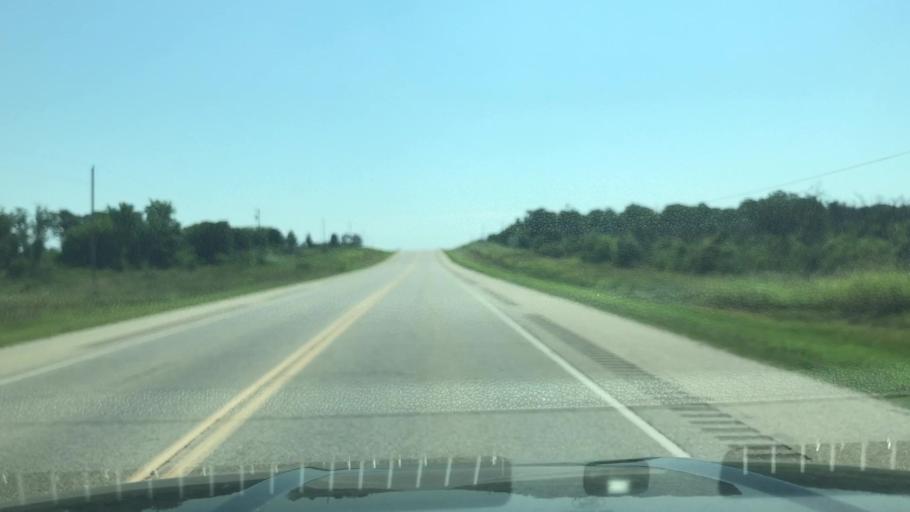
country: US
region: Oklahoma
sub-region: Creek County
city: Mannford
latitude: 36.0030
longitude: -96.4377
